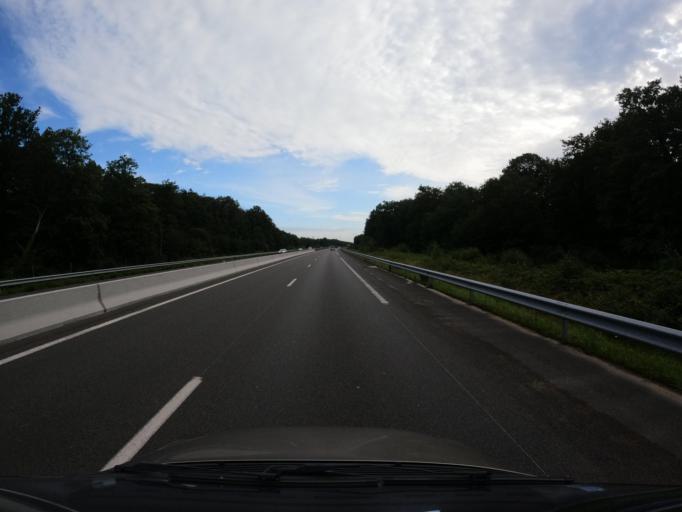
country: FR
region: Centre
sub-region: Departement d'Indre-et-Loire
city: Restigne
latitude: 47.2947
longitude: 0.2870
